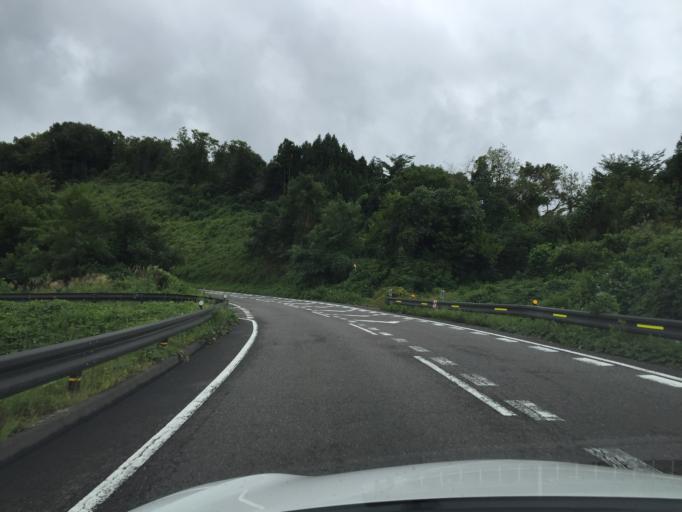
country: JP
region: Fukushima
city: Miharu
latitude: 37.4535
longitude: 140.5250
